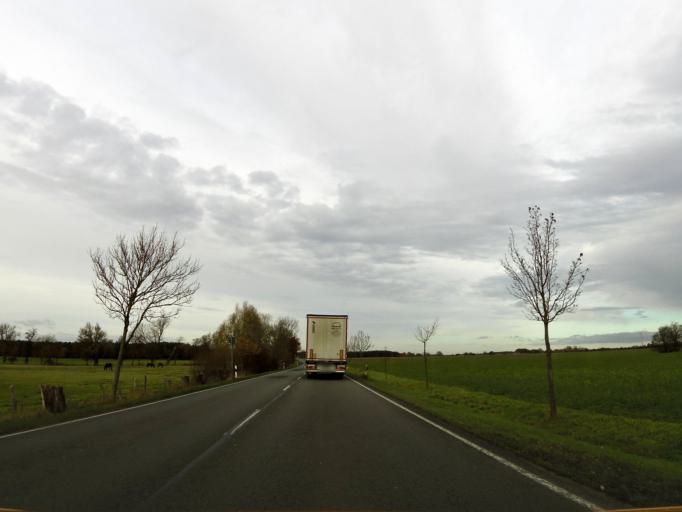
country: DE
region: Saxony-Anhalt
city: Pretzier
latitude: 52.7426
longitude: 11.2427
